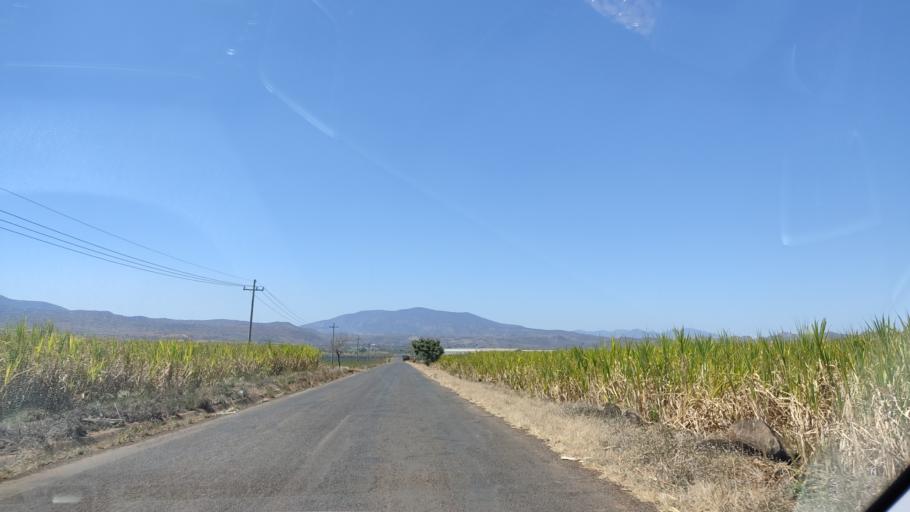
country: MX
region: Nayarit
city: Santa Maria del Oro
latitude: 21.4347
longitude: -104.6187
